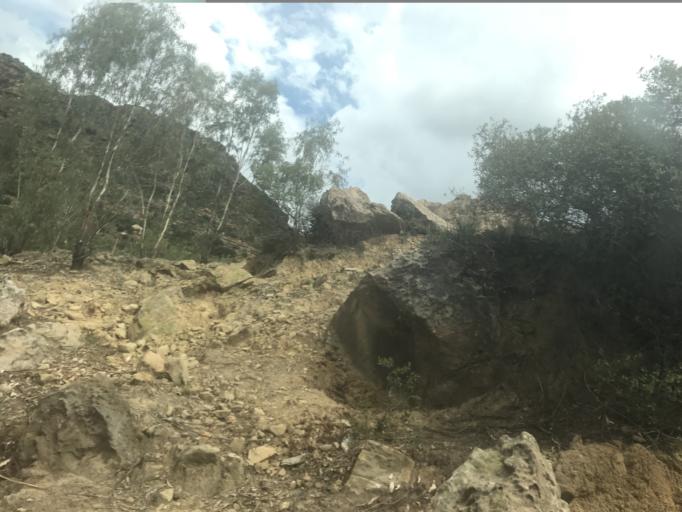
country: LS
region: Maseru
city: Nako
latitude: -29.6324
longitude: 27.5138
